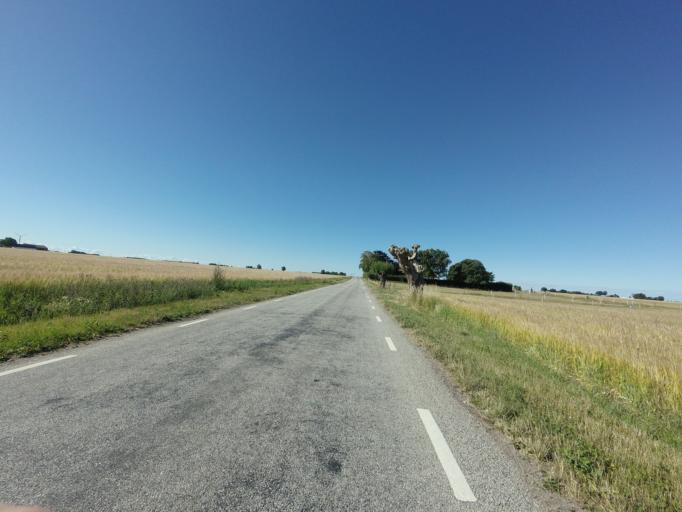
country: SE
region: Skane
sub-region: Trelleborgs Kommun
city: Skare
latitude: 55.4016
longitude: 13.0192
